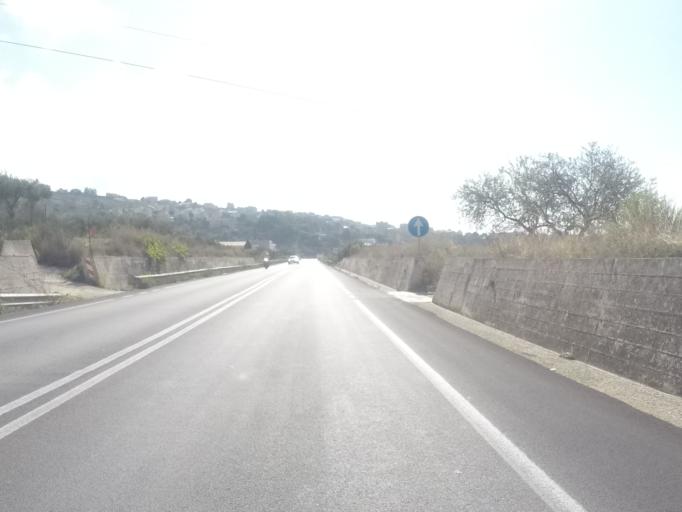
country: IT
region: Sicily
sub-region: Agrigento
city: Sciacca
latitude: 37.5159
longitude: 13.0894
